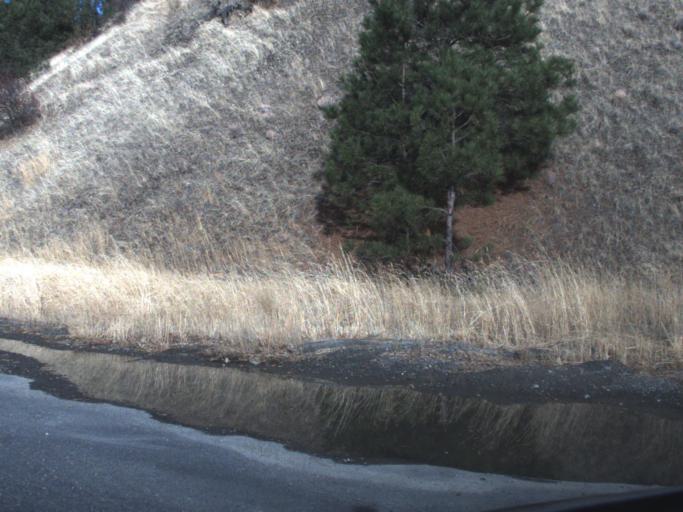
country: US
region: Washington
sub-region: Stevens County
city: Kettle Falls
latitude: 48.3615
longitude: -118.1629
